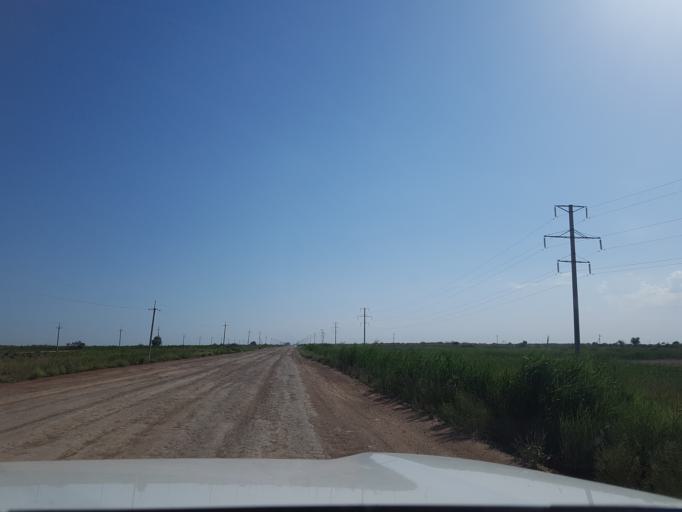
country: TM
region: Dasoguz
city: Koeneuergench
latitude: 42.1156
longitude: 58.9245
